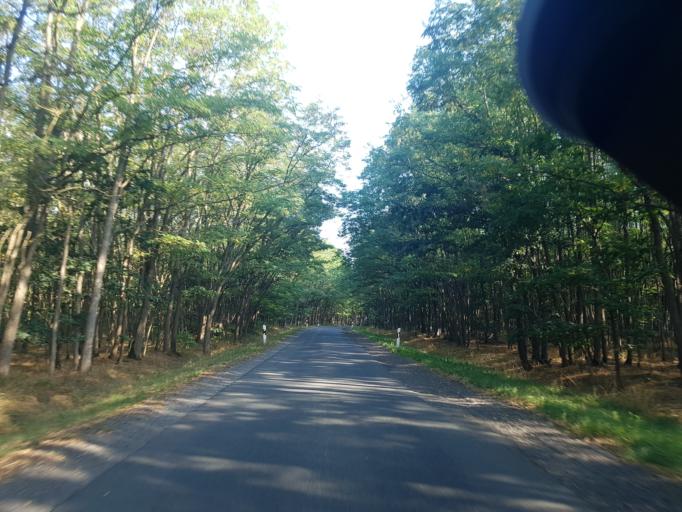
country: DE
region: Brandenburg
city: Niemegk
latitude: 52.0047
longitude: 12.6826
